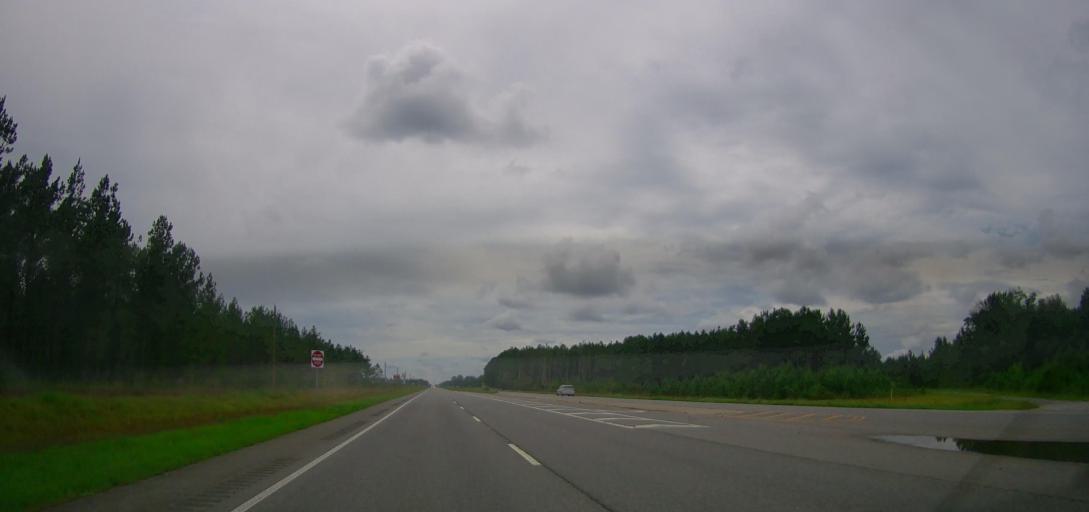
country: US
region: Georgia
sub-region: Appling County
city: Baxley
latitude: 31.7327
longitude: -82.2177
